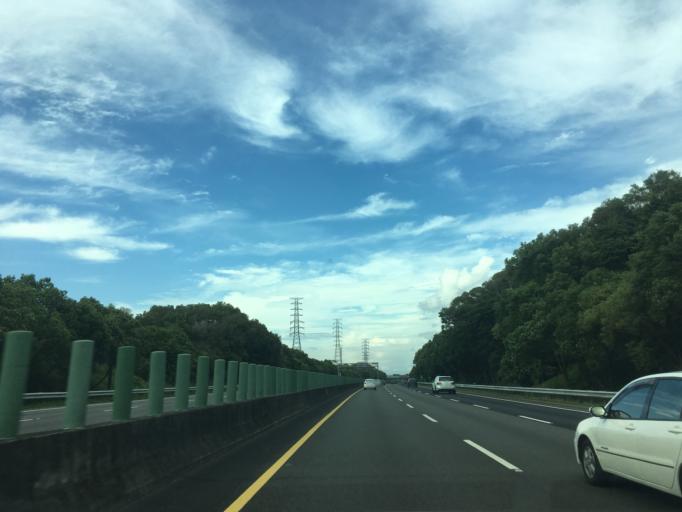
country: TW
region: Taiwan
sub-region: Chiayi
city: Jiayi Shi
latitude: 23.5820
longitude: 120.5116
